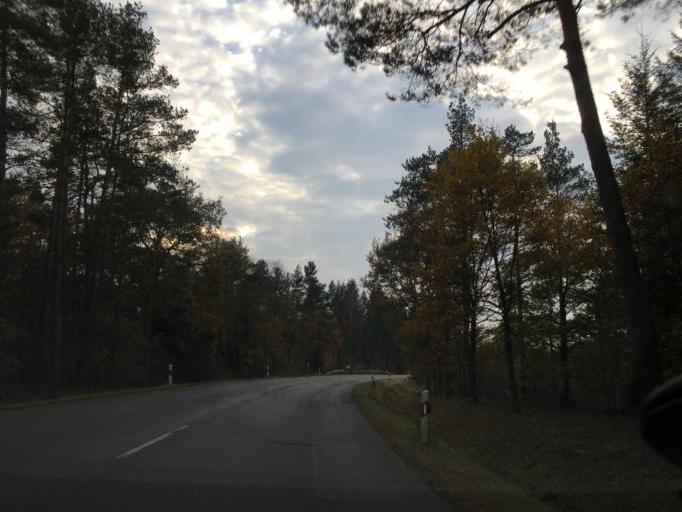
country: DE
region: Lower Saxony
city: Wietzendorf
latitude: 52.9880
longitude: 9.9915
